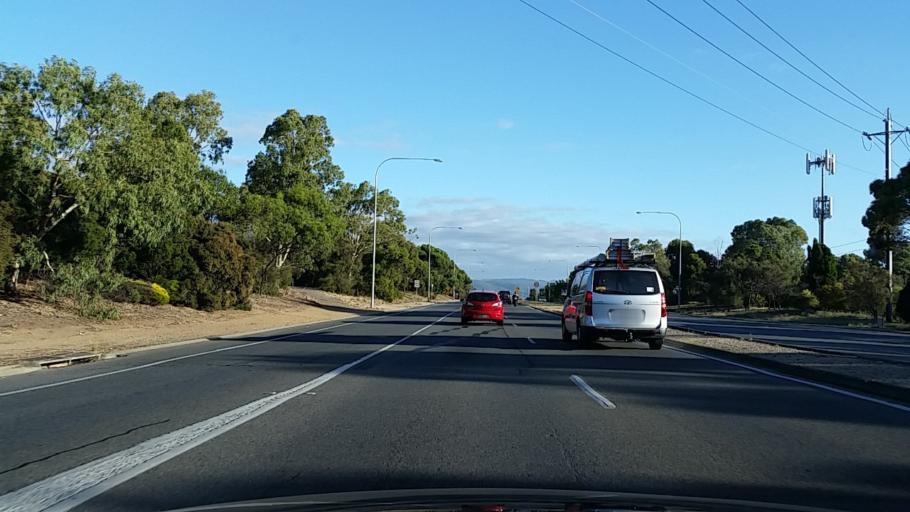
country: AU
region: South Australia
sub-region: Tea Tree Gully
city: Modbury
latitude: -34.8121
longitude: 138.6752
